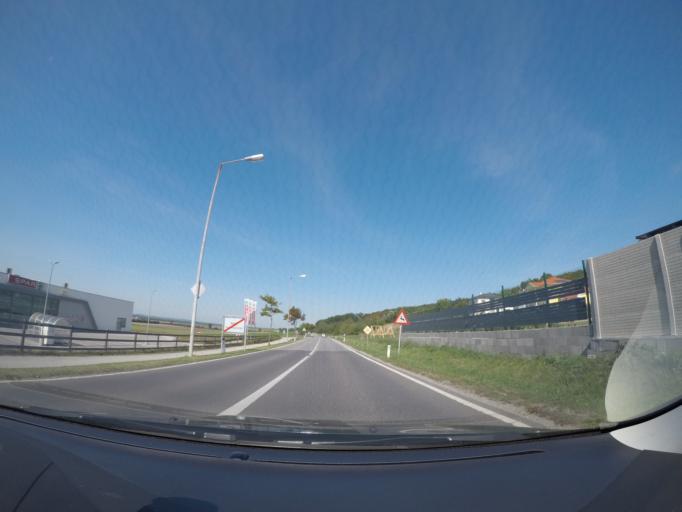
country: AT
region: Lower Austria
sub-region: Politischer Bezirk Bruck an der Leitha
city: Hof am Leithaberge
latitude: 47.9487
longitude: 16.5838
